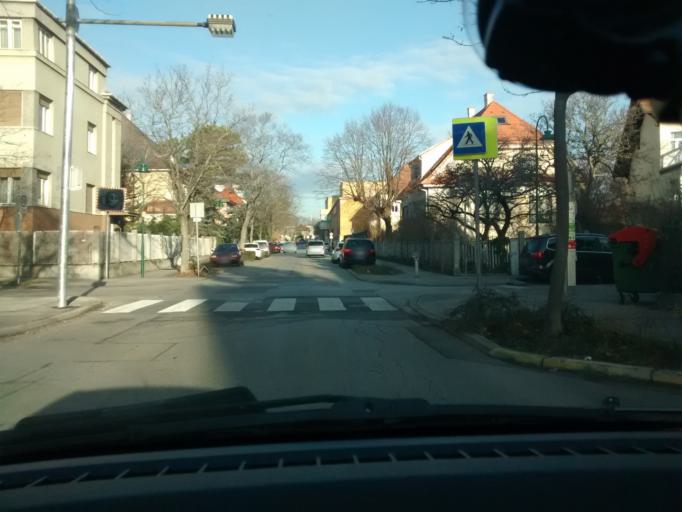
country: AT
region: Lower Austria
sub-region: Politischer Bezirk Modling
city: Modling
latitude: 48.0800
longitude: 16.2881
